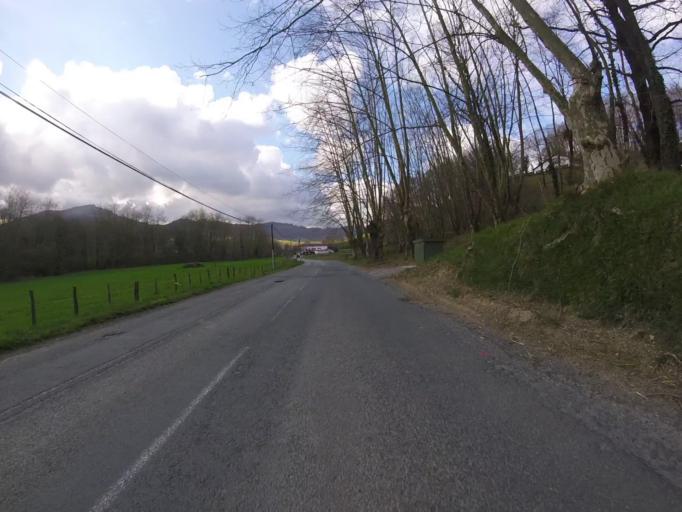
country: FR
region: Aquitaine
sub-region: Departement des Pyrenees-Atlantiques
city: Sare
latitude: 43.2935
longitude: -1.5777
